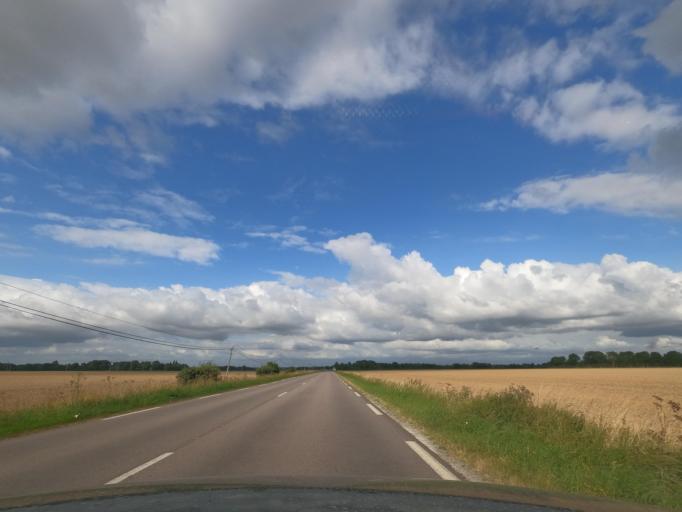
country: FR
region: Haute-Normandie
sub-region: Departement de l'Eure
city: Broglie
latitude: 48.9908
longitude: 0.5028
